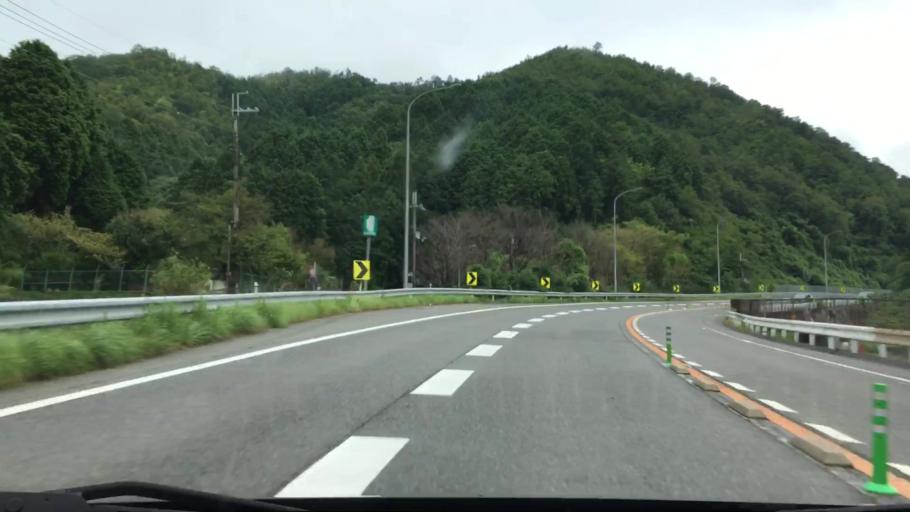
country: JP
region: Hyogo
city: Himeji
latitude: 35.0015
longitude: 134.7680
